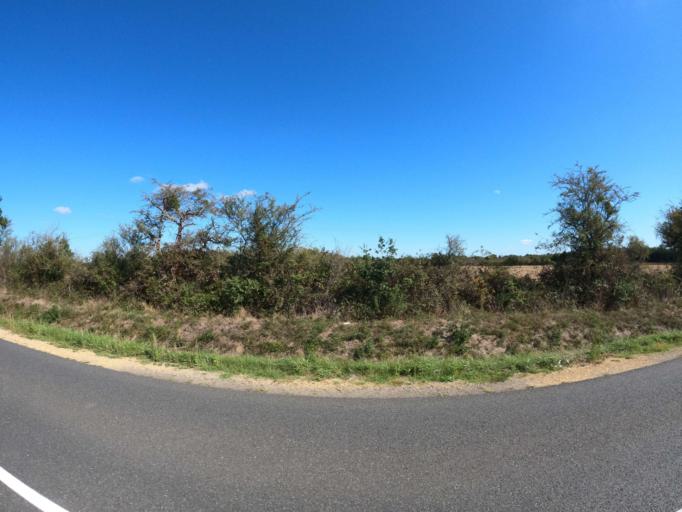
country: FR
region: Poitou-Charentes
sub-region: Departement de la Vienne
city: Saulge
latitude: 46.3818
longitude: 0.9193
